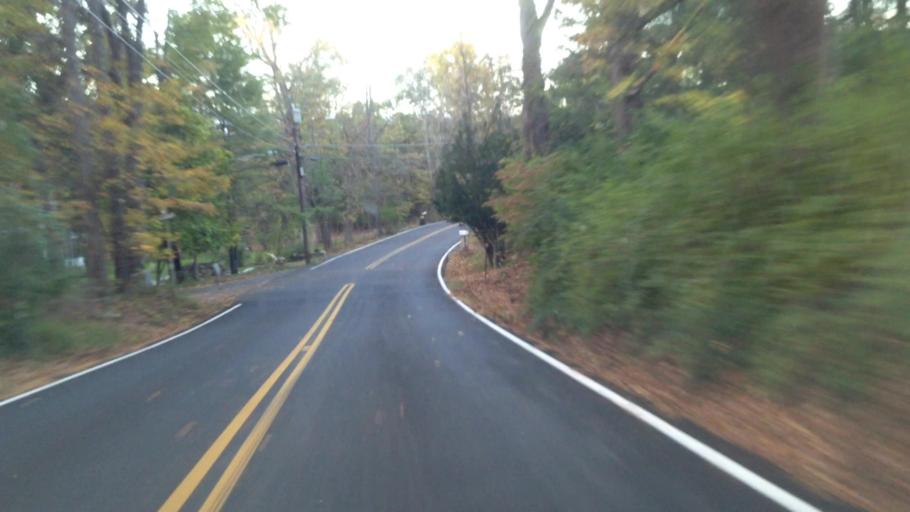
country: US
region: New York
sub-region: Ulster County
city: Tillson
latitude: 41.8296
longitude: -74.0402
